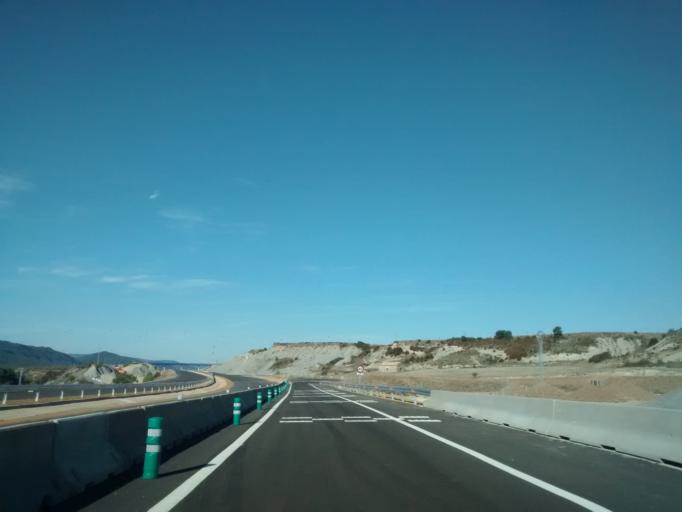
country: ES
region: Aragon
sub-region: Provincia de Huesca
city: Santa Cruz de la Seros
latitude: 42.5651
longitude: -0.7113
